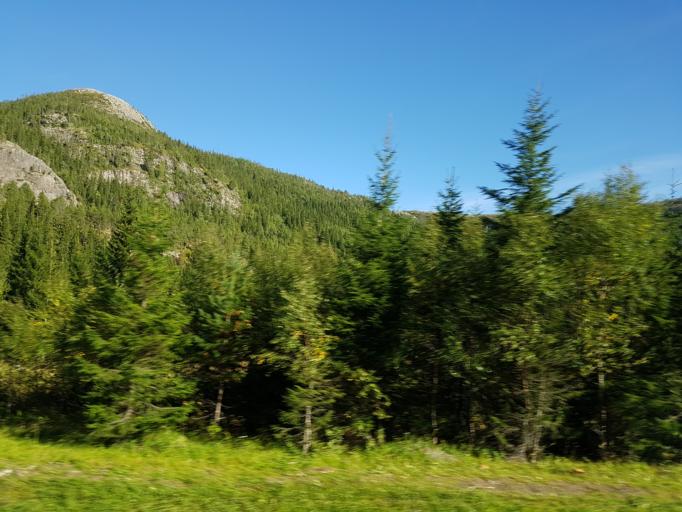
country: NO
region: Sor-Trondelag
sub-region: Afjord
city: A i Afjord
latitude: 63.7314
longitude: 10.2345
